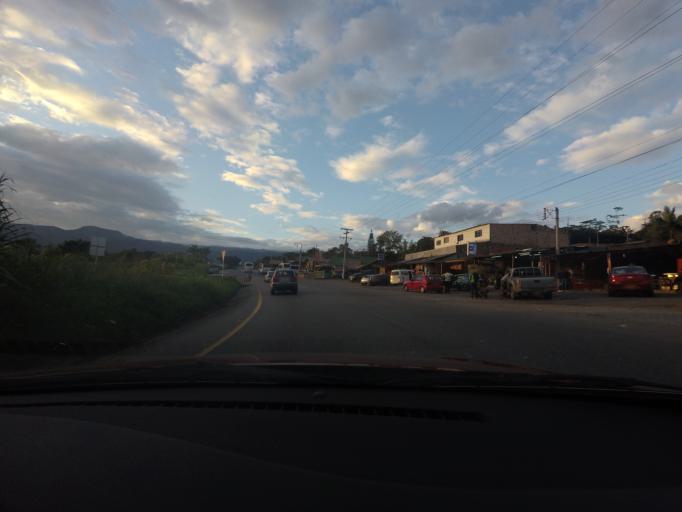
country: CO
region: Cundinamarca
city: Silvania
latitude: 4.3678
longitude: -74.3824
